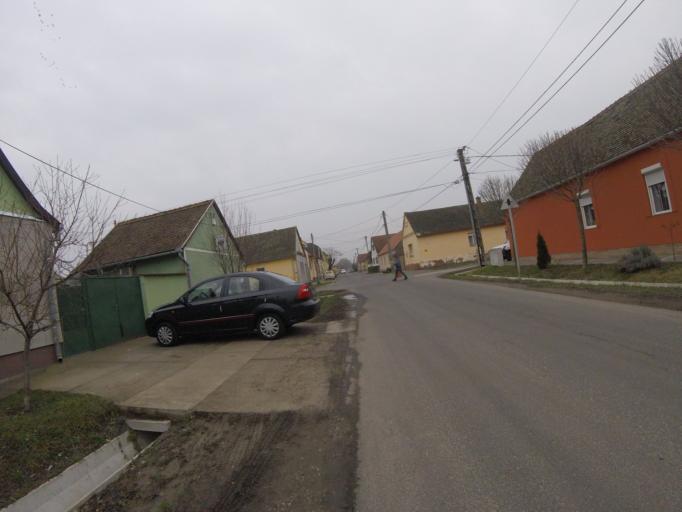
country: HU
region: Baranya
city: Mohacs
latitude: 45.9979
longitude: 18.6856
